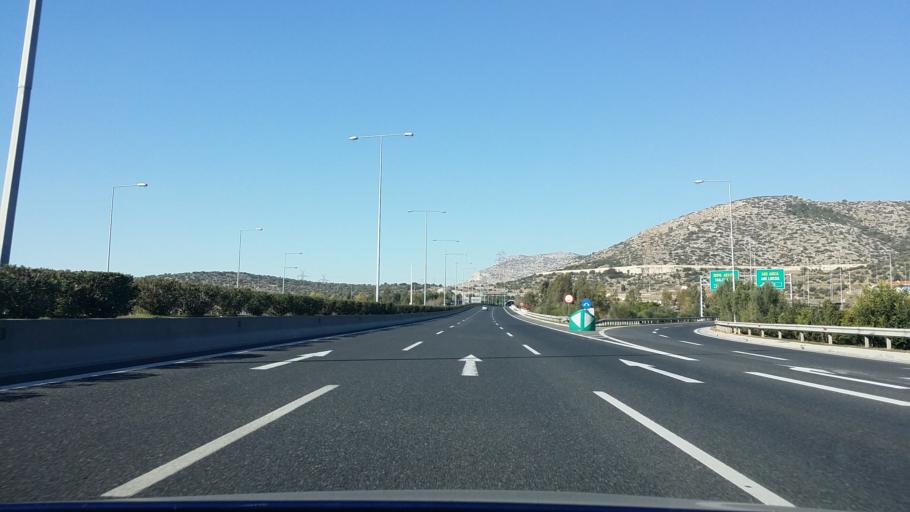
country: GR
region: Attica
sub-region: Nomarchia Dytikis Attikis
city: Ano Liosia
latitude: 38.0770
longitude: 23.6814
